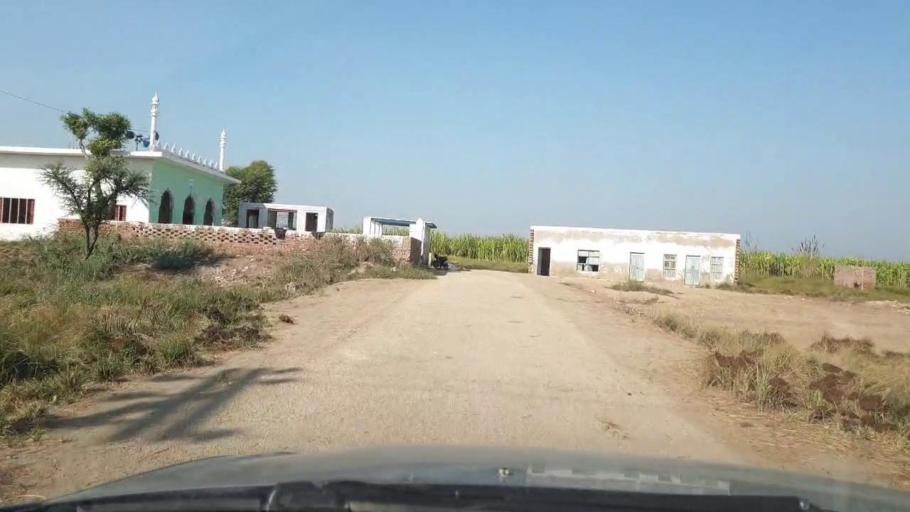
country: PK
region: Sindh
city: Tando Muhammad Khan
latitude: 25.1163
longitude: 68.5898
